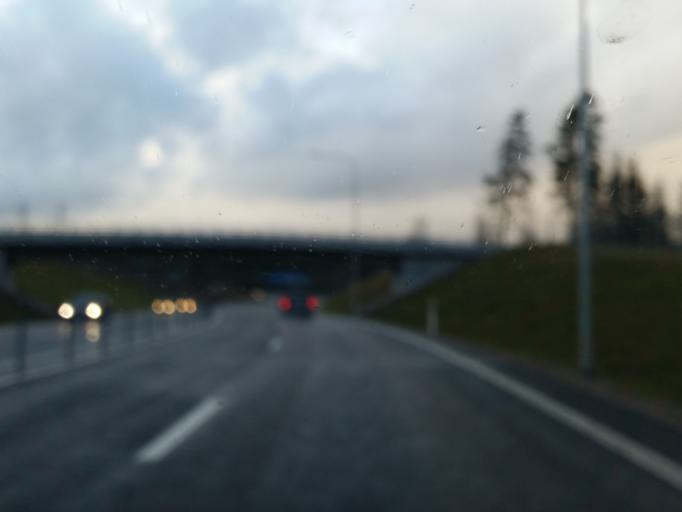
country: SE
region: Vaestra Goetaland
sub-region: Boras Kommun
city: Sjomarken
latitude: 57.7089
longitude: 12.8715
